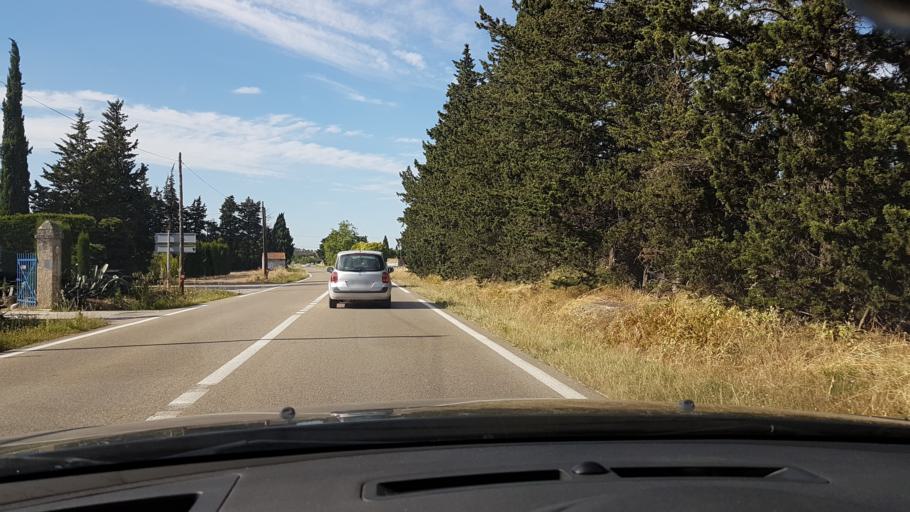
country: FR
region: Provence-Alpes-Cote d'Azur
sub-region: Departement des Bouches-du-Rhone
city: Graveson
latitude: 43.8560
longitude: 4.7685
